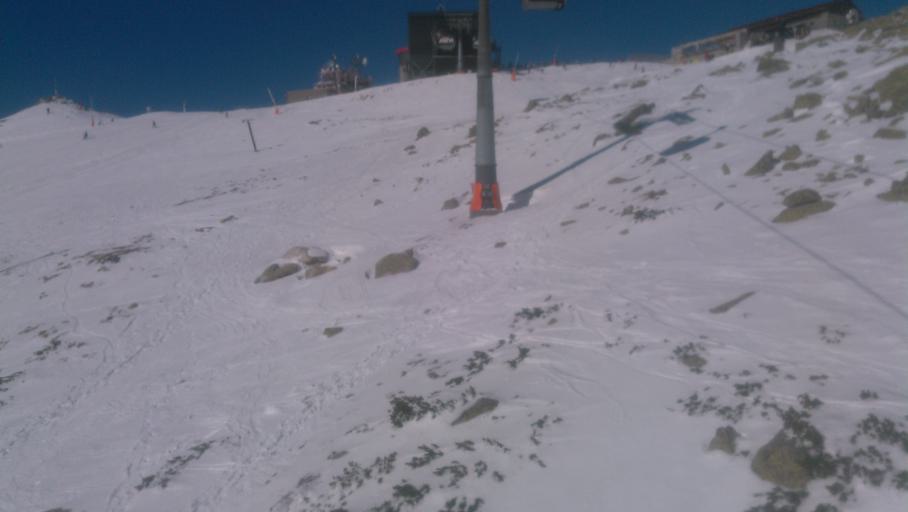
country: SK
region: Zilinsky
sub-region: Okres Liptovsky Mikulas
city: Liptovsky Mikulas
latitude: 48.9416
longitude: 19.5917
